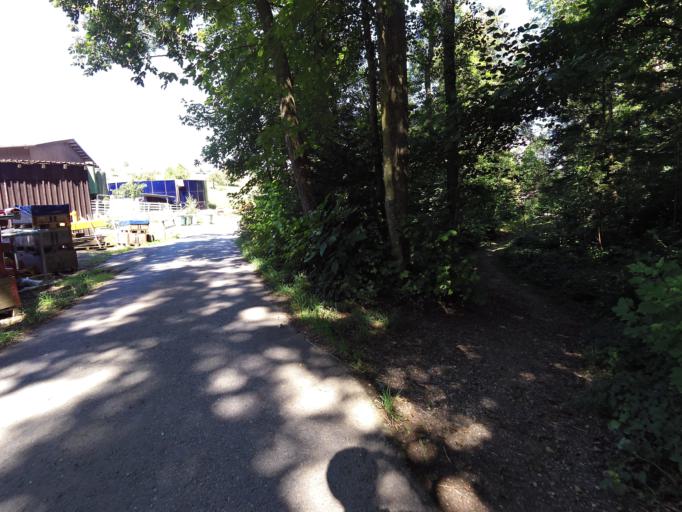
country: CH
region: Thurgau
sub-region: Kreuzlingen District
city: Tagerwilen
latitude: 47.6534
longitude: 9.1226
